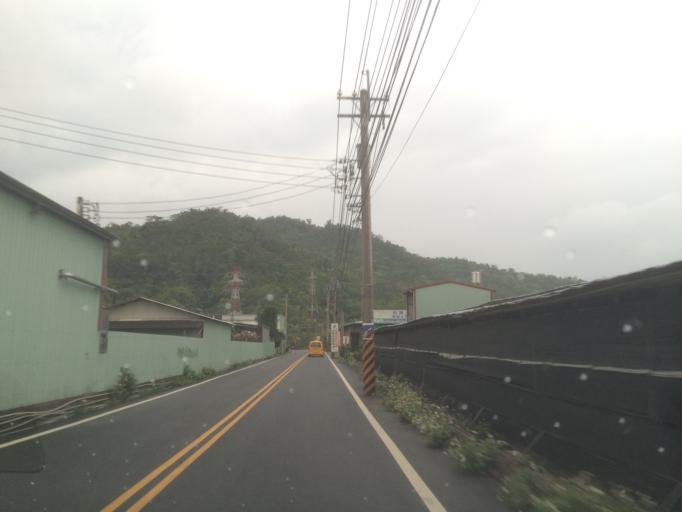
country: TW
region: Taiwan
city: Fengyuan
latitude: 24.1814
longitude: 120.8192
